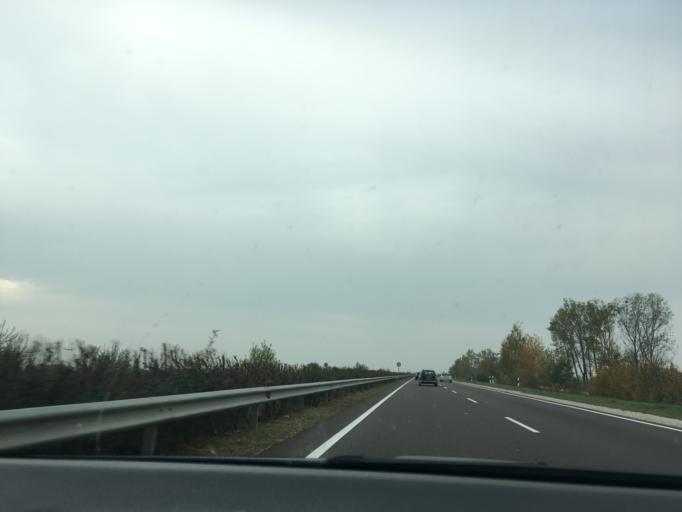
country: HU
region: Pest
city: Tortel
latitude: 47.1906
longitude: 19.8875
